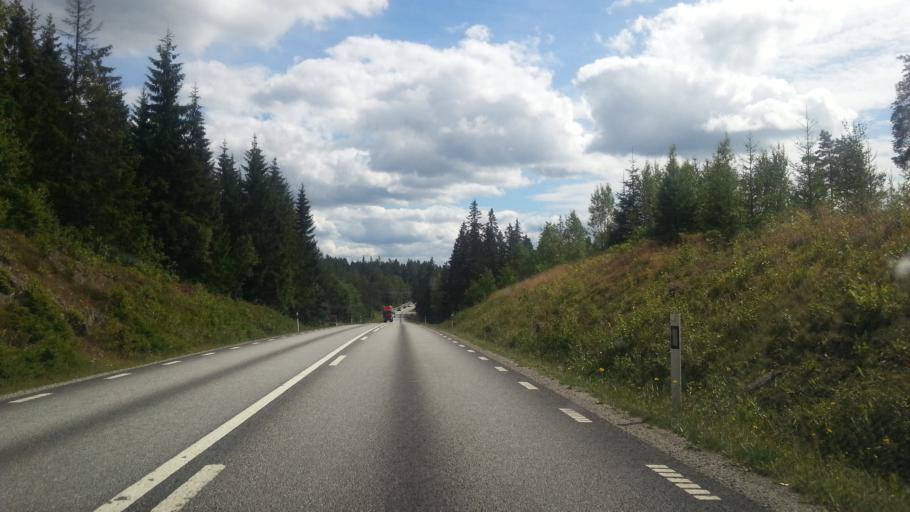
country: SE
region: OErebro
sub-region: Lindesbergs Kommun
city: Stora
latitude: 59.6487
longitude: 15.1212
